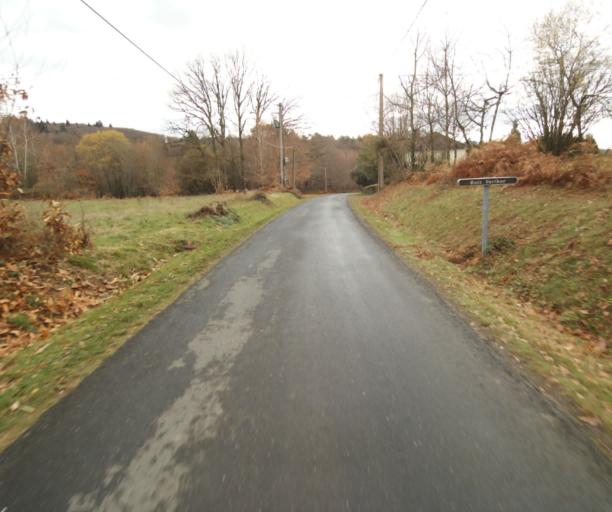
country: FR
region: Limousin
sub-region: Departement de la Correze
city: Saint-Mexant
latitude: 45.2796
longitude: 1.6339
